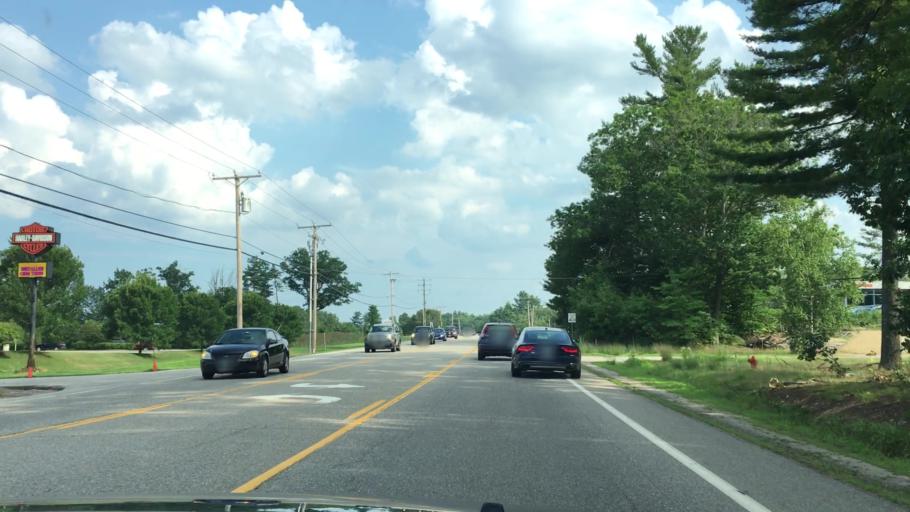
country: US
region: New Hampshire
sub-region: Strafford County
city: Rochester
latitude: 43.3295
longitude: -71.0053
